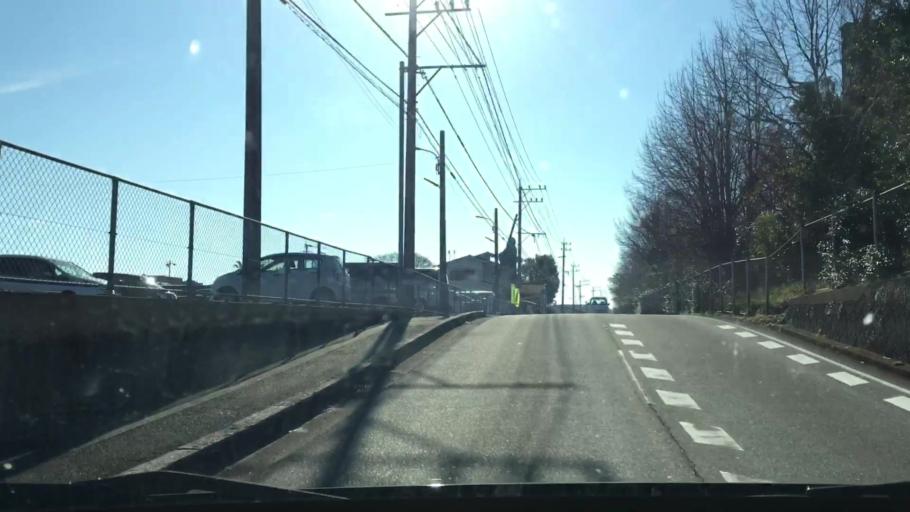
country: JP
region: Kagoshima
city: Kajiki
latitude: 31.7991
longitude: 130.7140
